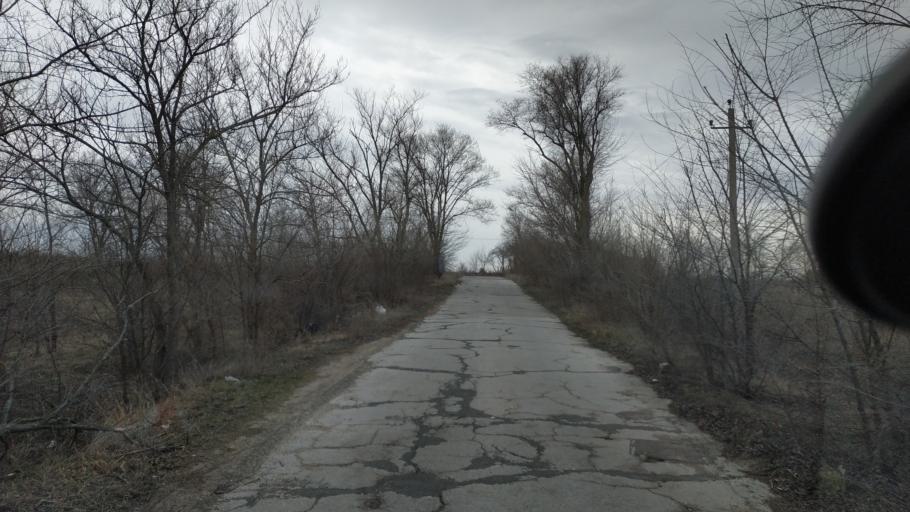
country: MD
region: Telenesti
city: Cocieri
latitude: 47.3253
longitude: 29.0963
